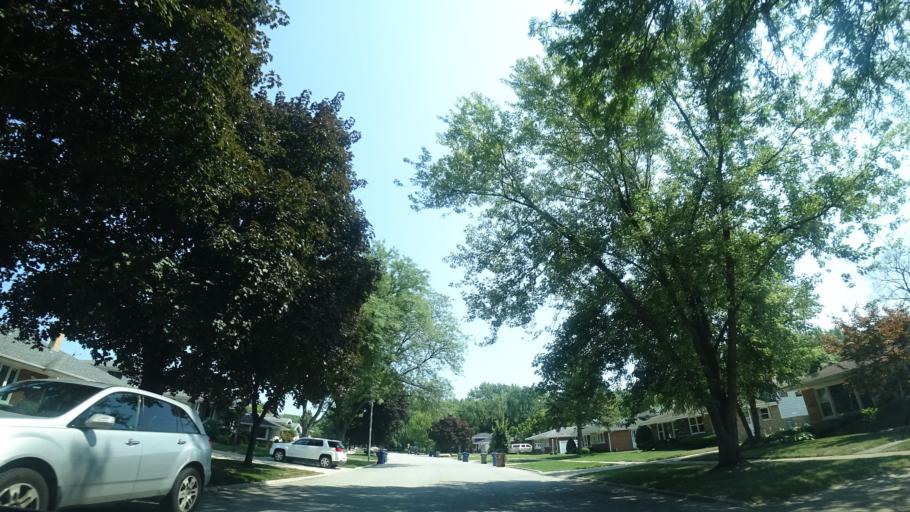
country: US
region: Illinois
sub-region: Cook County
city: Oak Lawn
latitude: 41.6954
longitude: -87.7485
